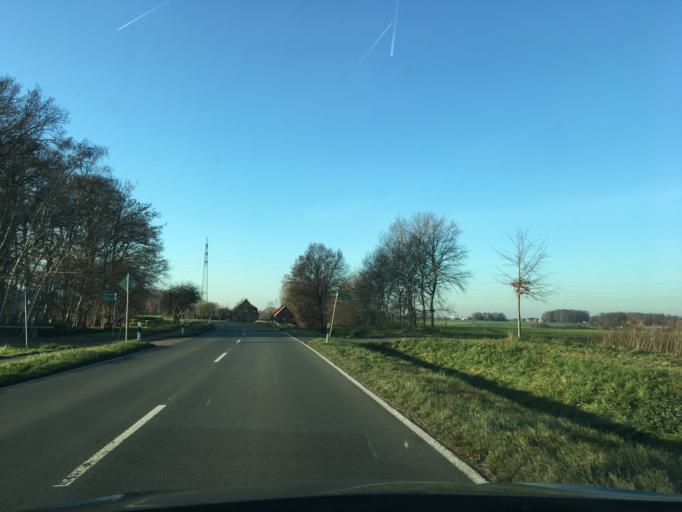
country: DE
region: North Rhine-Westphalia
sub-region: Regierungsbezirk Munster
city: Ahaus
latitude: 52.1180
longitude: 6.9361
